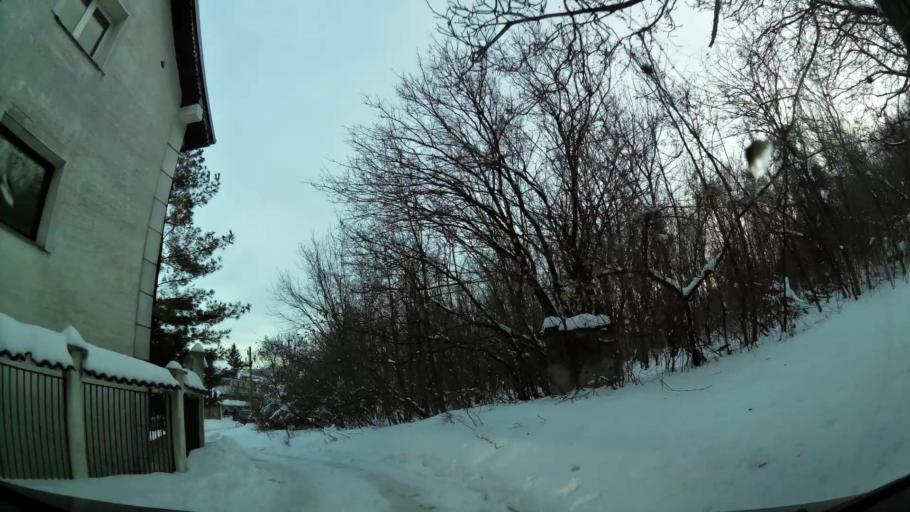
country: RS
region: Central Serbia
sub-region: Belgrade
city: Palilula
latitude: 44.7962
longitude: 20.5167
